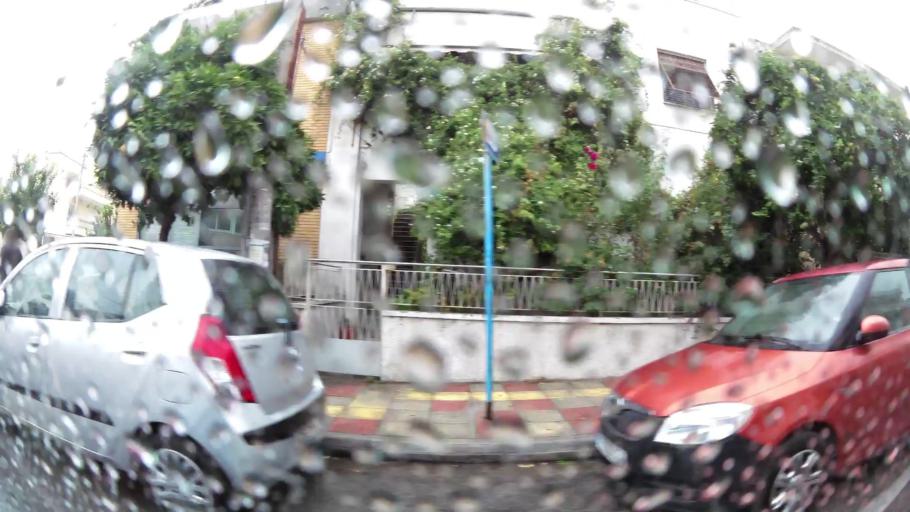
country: GR
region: Attica
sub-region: Nomarchia Athinas
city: Ymittos
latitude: 37.9551
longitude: 23.7446
